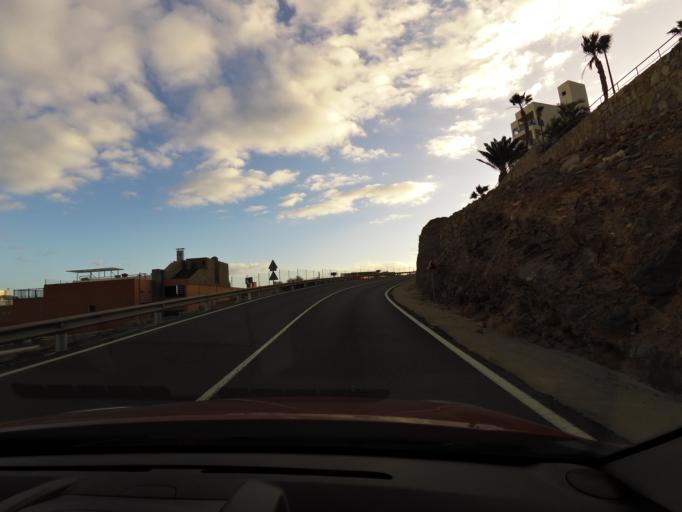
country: ES
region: Canary Islands
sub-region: Provincia de Las Palmas
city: Puerto Rico
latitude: 27.7996
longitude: -15.7332
